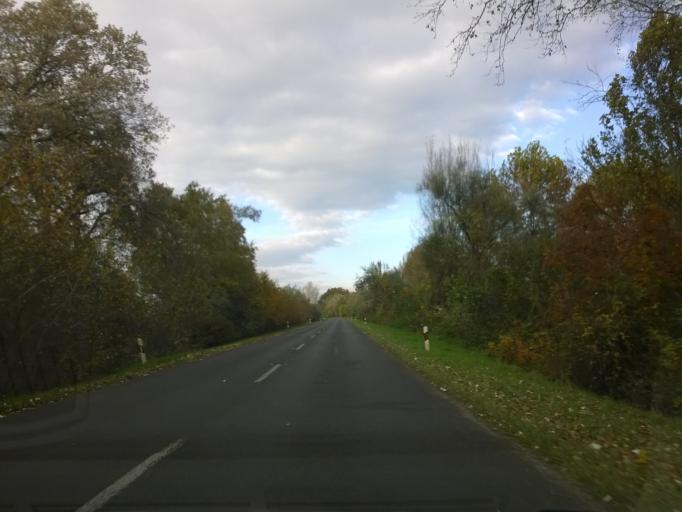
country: HU
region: Pest
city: Rackeve
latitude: 47.1969
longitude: 18.9437
